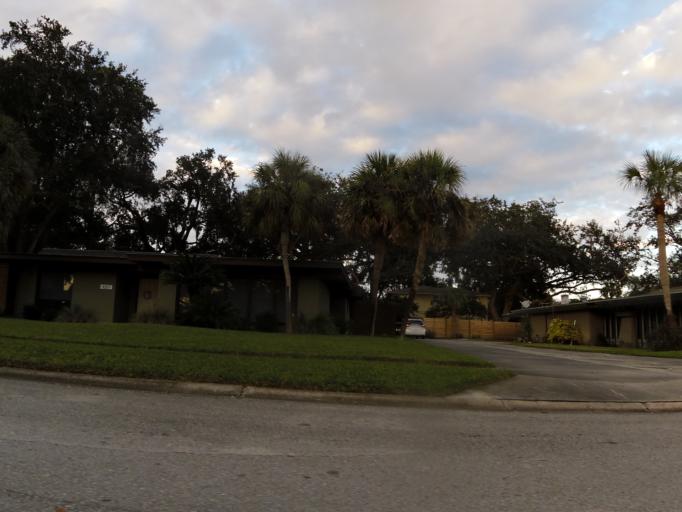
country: US
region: Florida
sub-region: Duval County
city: Jacksonville
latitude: 30.2770
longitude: -81.6624
